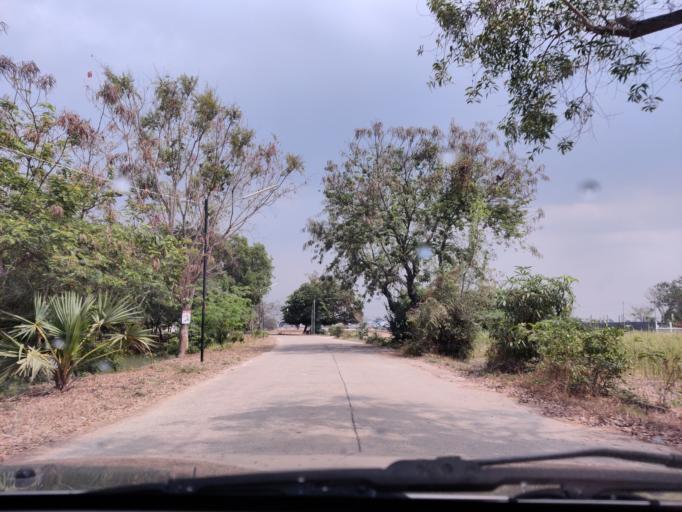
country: TH
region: Sisaket
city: Si Sa Ket
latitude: 15.1026
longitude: 104.3509
